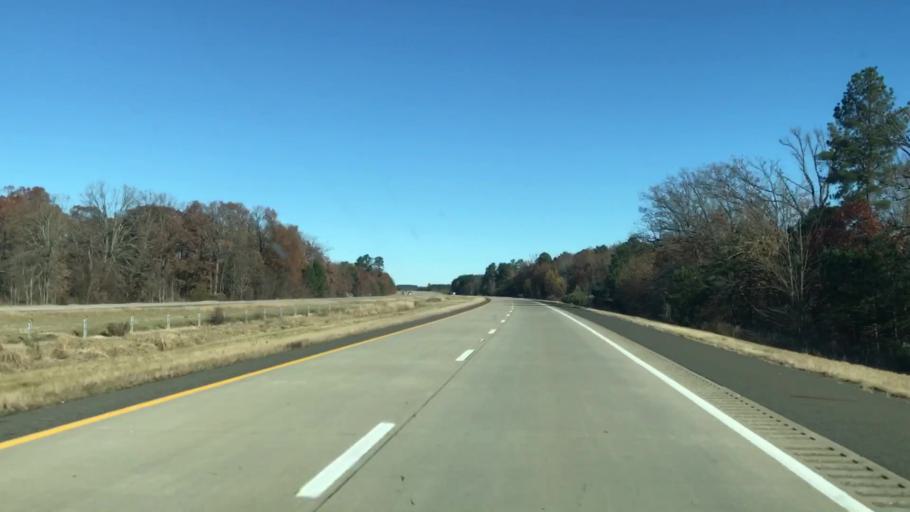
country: US
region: Texas
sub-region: Bowie County
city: Texarkana
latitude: 33.2121
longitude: -93.8739
